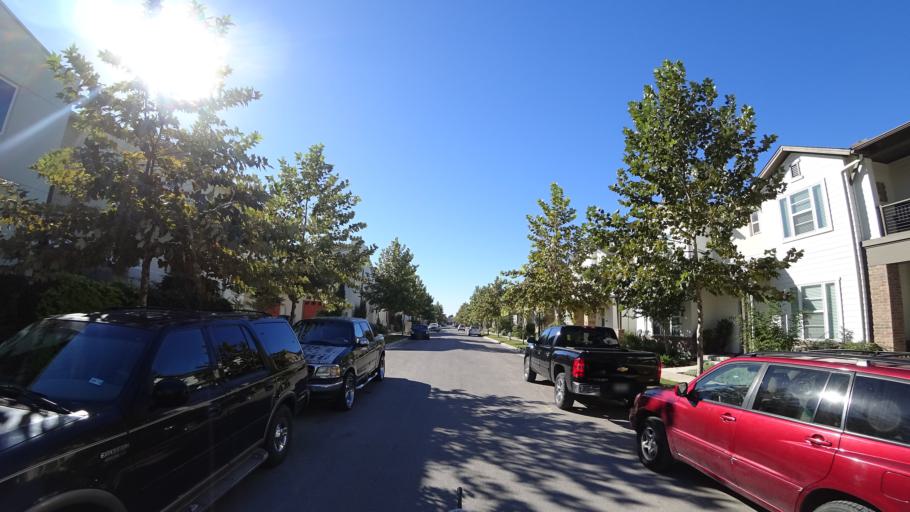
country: US
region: Texas
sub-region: Travis County
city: Austin
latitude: 30.3010
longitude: -97.7013
